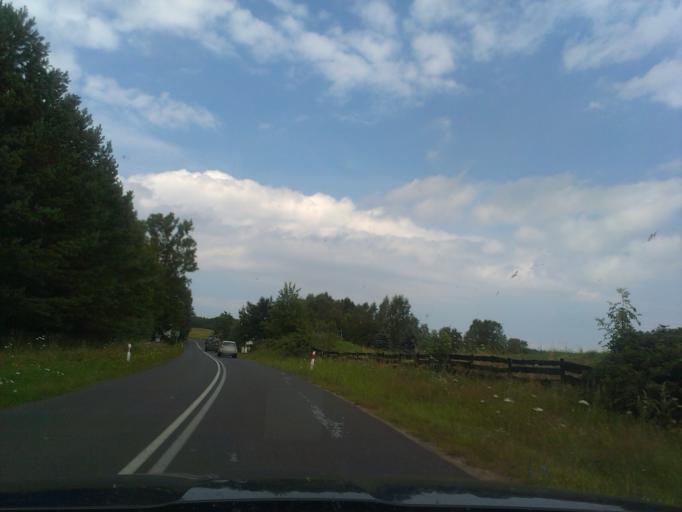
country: PL
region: West Pomeranian Voivodeship
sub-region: Powiat kamienski
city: Wolin
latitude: 53.9688
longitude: 14.6035
